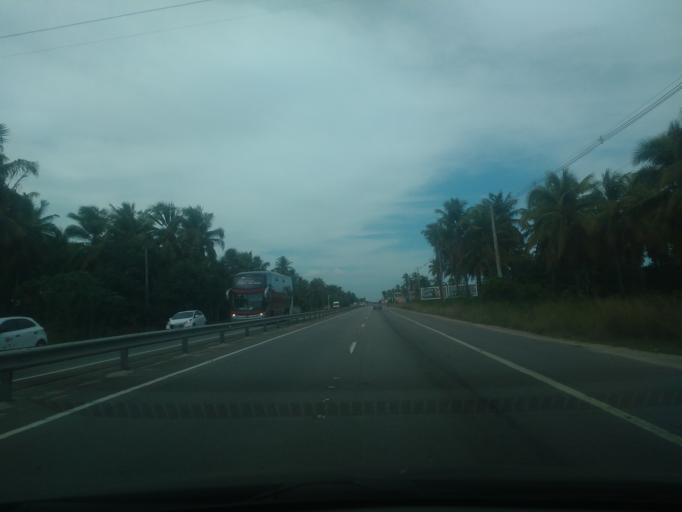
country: BR
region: Alagoas
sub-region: Marechal Deodoro
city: Marechal Deodoro
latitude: -9.7119
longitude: -35.8208
